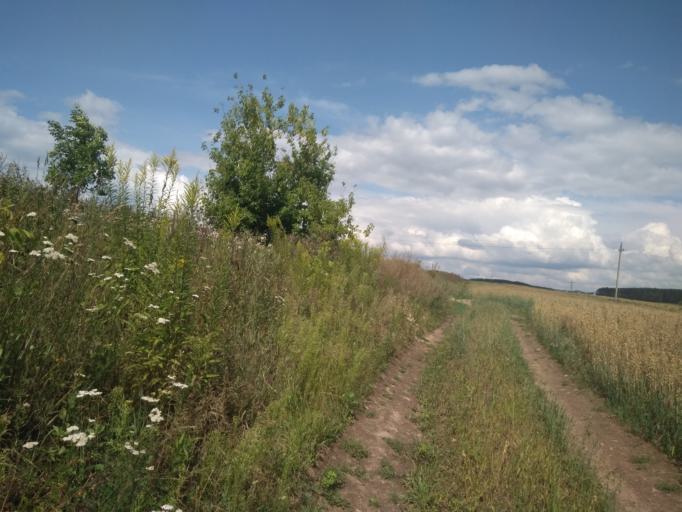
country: BY
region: Minsk
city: Minsk
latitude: 53.9435
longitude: 27.5563
